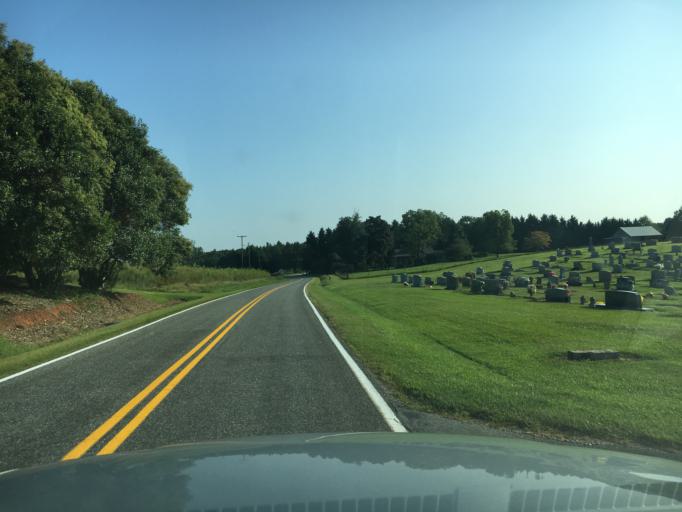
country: US
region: North Carolina
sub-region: Polk County
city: Columbus
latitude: 35.2303
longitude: -82.0510
